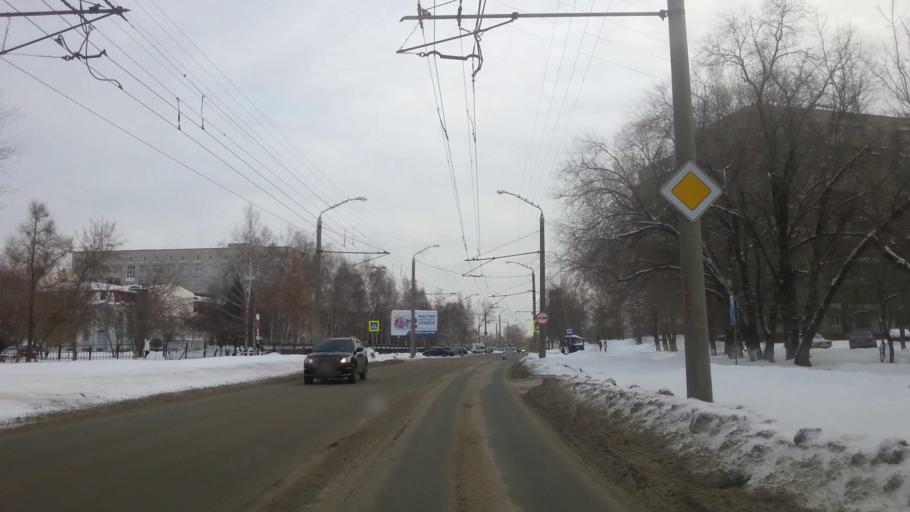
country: RU
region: Altai Krai
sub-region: Gorod Barnaulskiy
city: Barnaul
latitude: 53.3689
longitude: 83.7030
